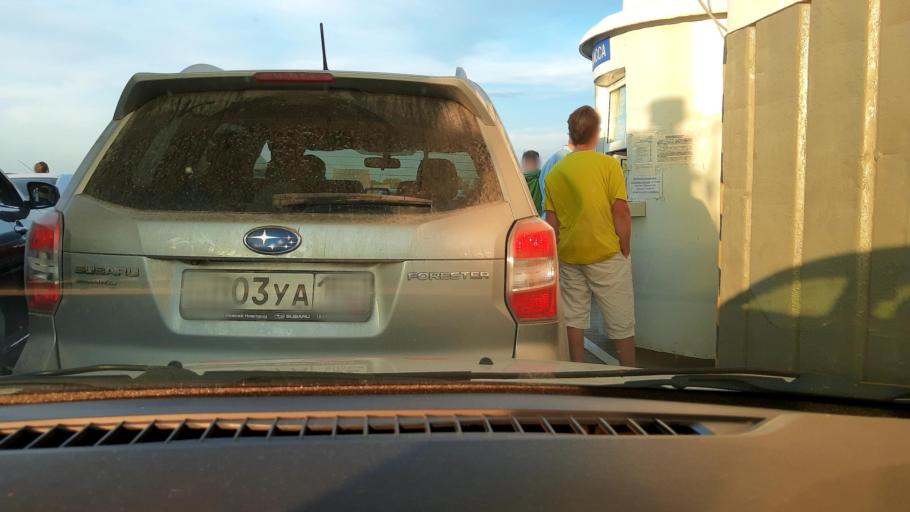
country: RU
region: Nizjnij Novgorod
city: Nizhniy Novgorod
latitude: 56.3383
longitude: 44.0330
